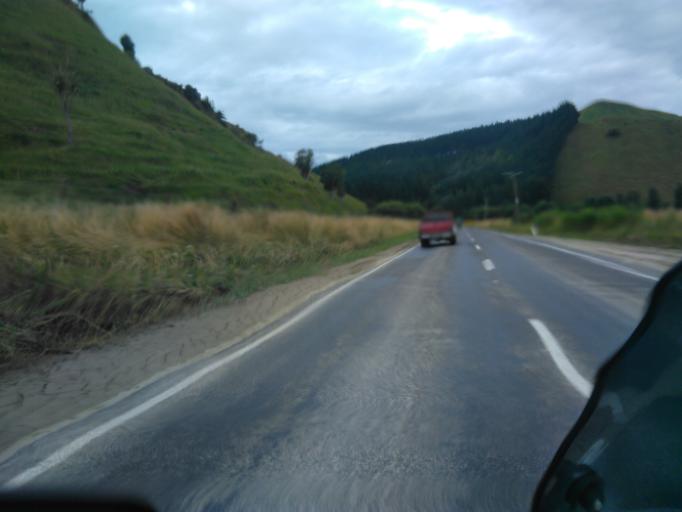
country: NZ
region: Gisborne
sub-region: Gisborne District
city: Gisborne
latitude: -38.4615
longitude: 177.7418
